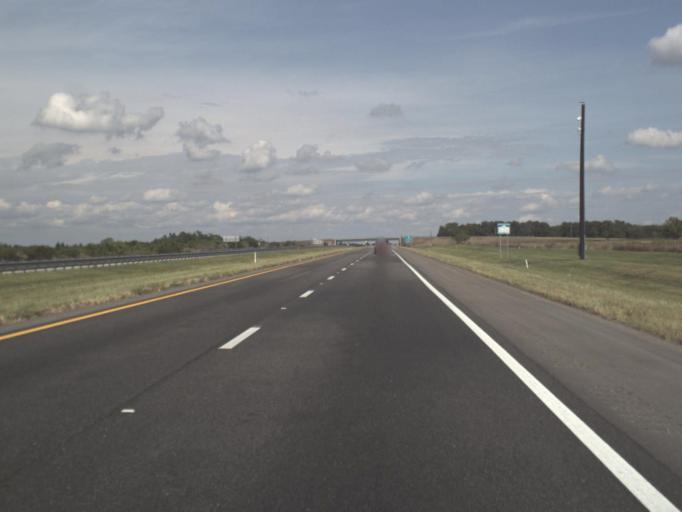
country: US
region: Florida
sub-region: Polk County
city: Fussels Corner
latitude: 28.0330
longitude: -81.8326
